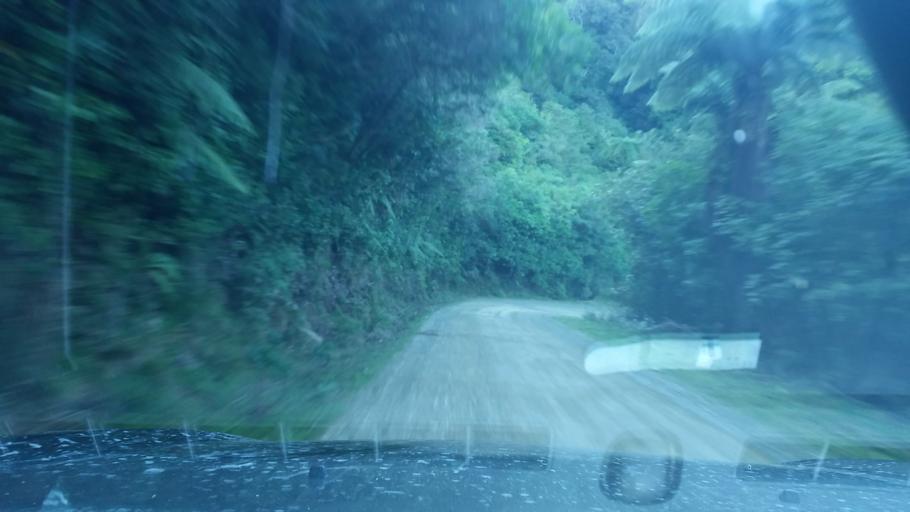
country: NZ
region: Marlborough
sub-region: Marlborough District
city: Picton
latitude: -41.0762
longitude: 174.1170
